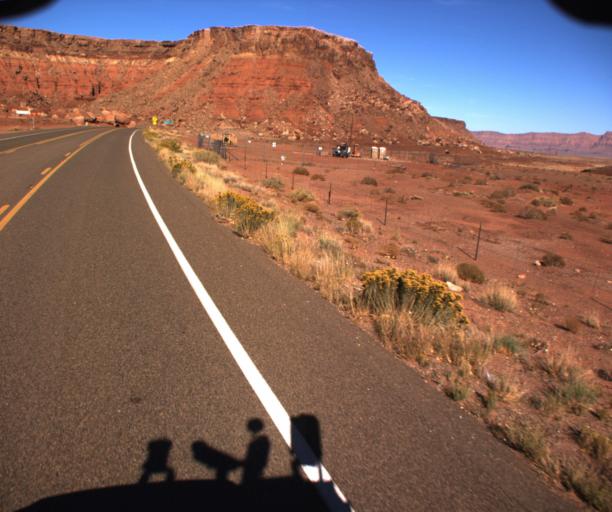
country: US
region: Arizona
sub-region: Coconino County
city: Page
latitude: 36.7437
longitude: -111.7529
